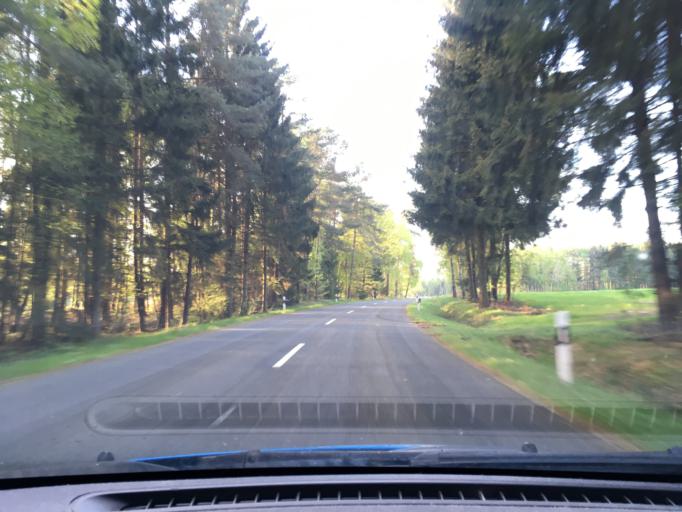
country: DE
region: Lower Saxony
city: Bispingen
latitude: 53.0049
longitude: 9.9965
